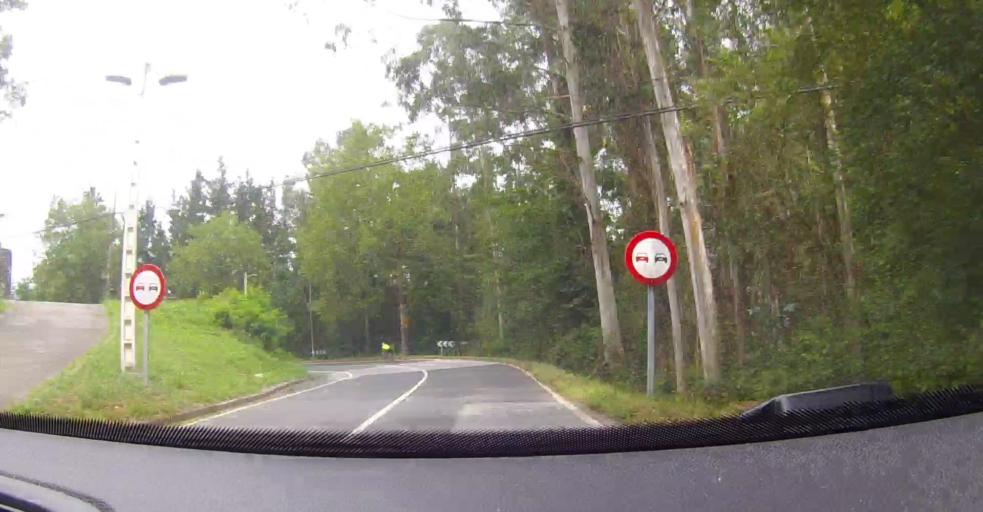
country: ES
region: Basque Country
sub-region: Bizkaia
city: Balmaseda
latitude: 43.2445
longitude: -3.2545
